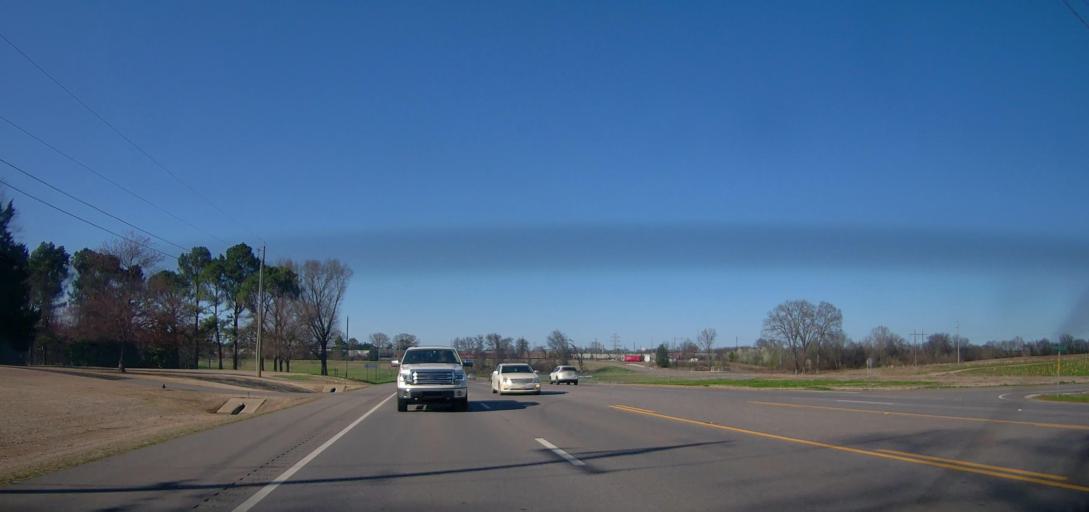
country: US
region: Alabama
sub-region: Colbert County
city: Muscle Shoals
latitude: 34.7095
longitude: -87.6348
